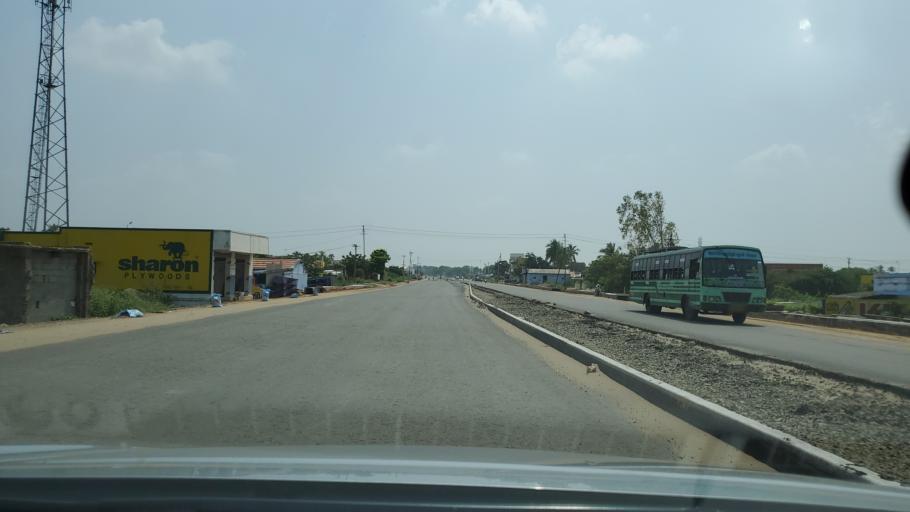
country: IN
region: Tamil Nadu
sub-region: Tiruppur
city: Dharapuram
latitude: 10.7687
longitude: 77.5131
